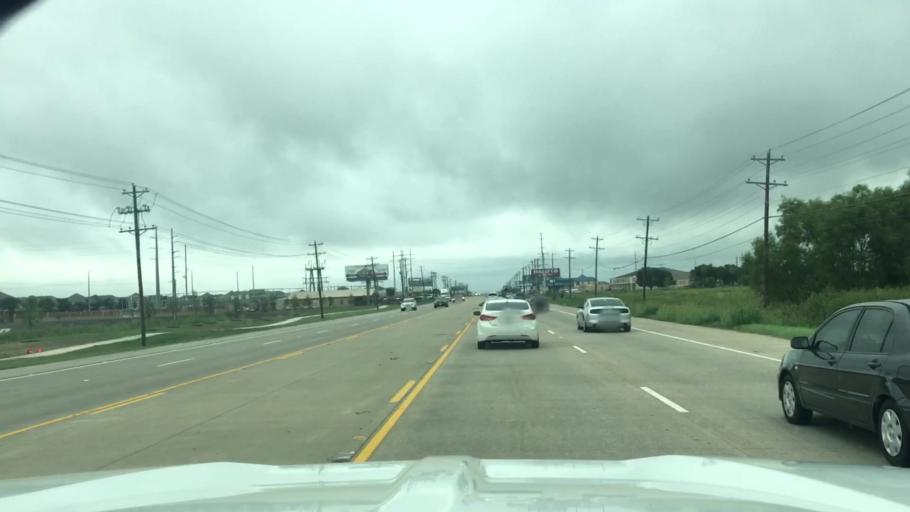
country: US
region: Texas
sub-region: Denton County
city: Little Elm
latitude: 33.2198
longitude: -96.9214
